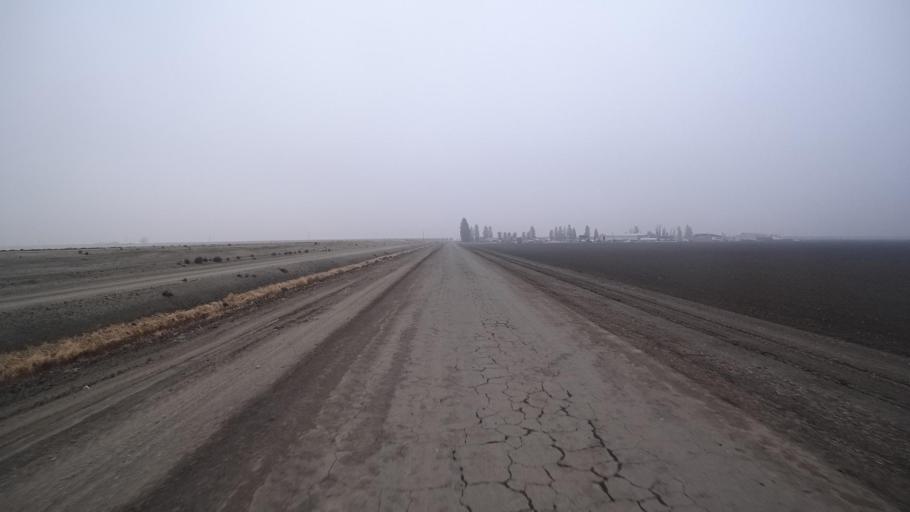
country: US
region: California
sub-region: Kern County
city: Buttonwillow
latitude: 35.4124
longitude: -119.5147
